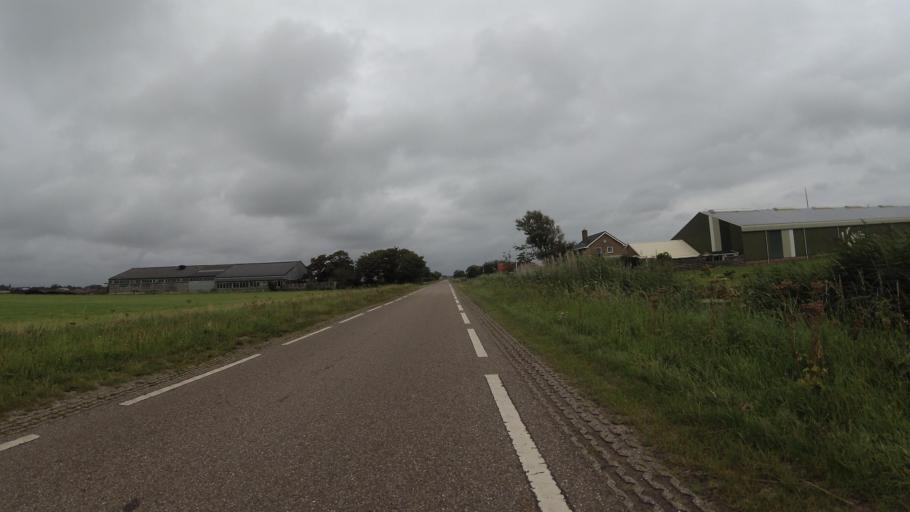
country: NL
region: North Holland
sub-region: Gemeente Den Helder
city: Den Helder
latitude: 52.9139
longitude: 4.7599
